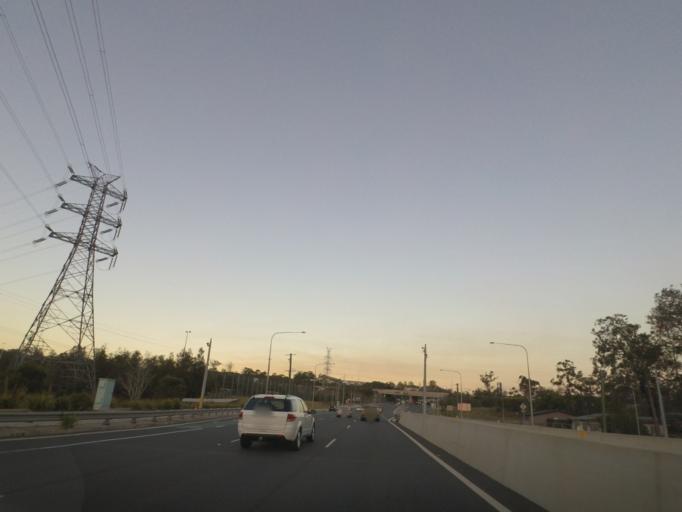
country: AU
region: Queensland
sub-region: Brisbane
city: Mackenzie
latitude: -27.5457
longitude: 153.1143
